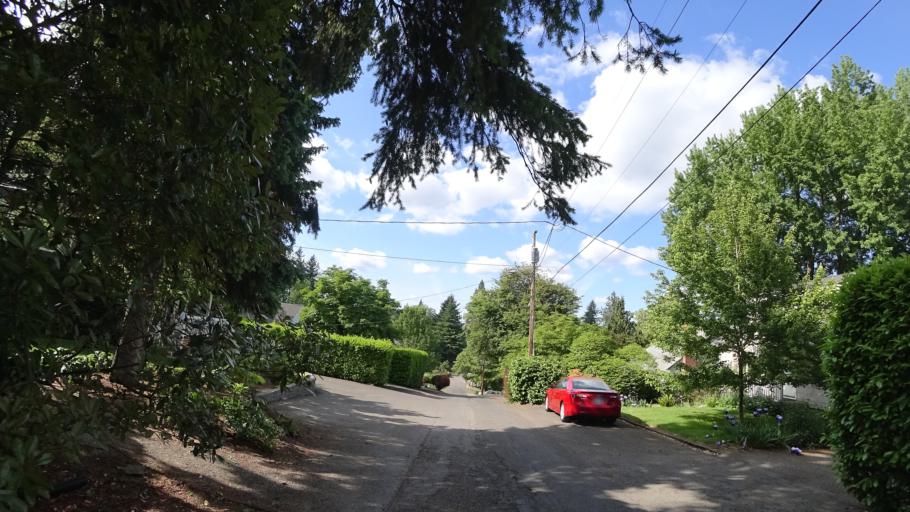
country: US
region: Oregon
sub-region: Washington County
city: Garden Home-Whitford
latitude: 45.4638
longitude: -122.7167
